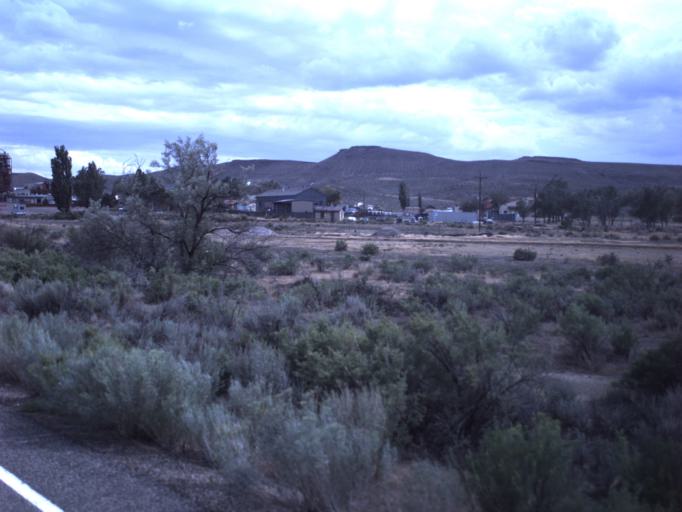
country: US
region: Colorado
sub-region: Rio Blanco County
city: Rangely
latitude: 40.0225
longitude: -109.1746
